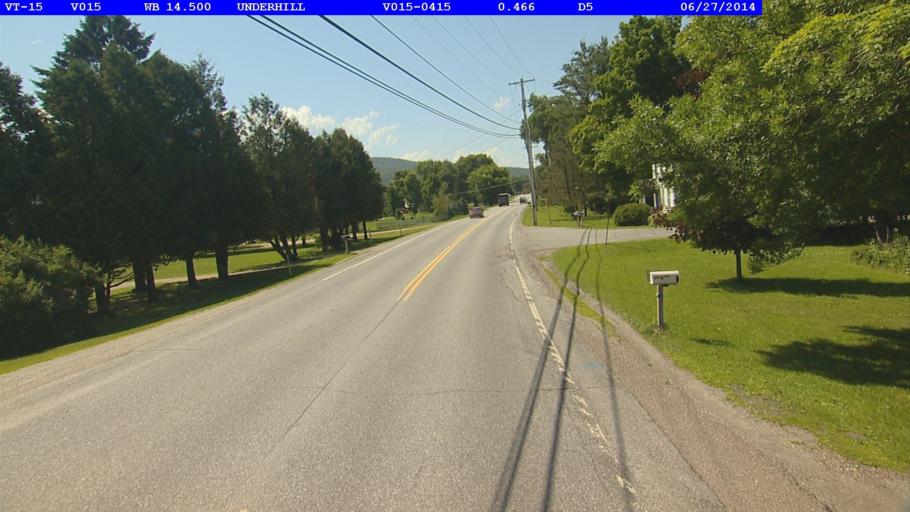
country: US
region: Vermont
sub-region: Chittenden County
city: Jericho
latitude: 44.5319
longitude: -72.9447
